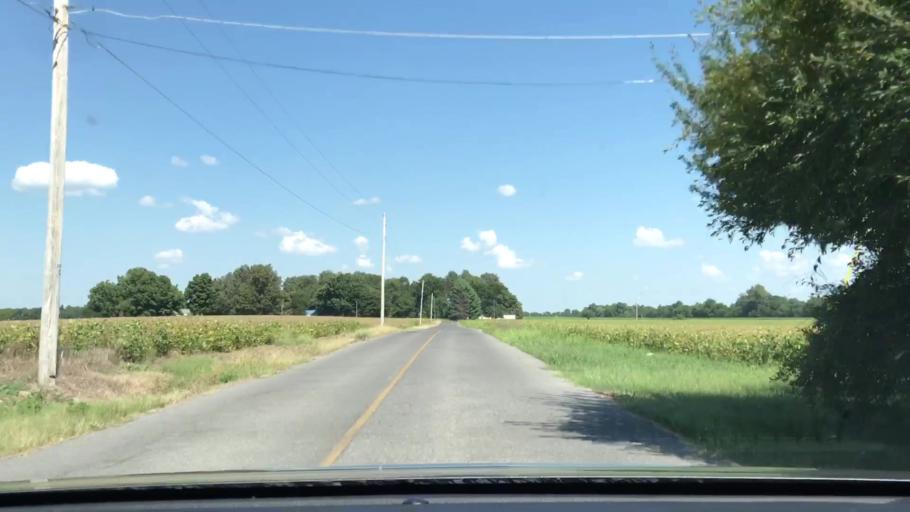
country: US
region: Kentucky
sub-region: Fulton County
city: Fulton
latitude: 36.5194
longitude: -88.9015
